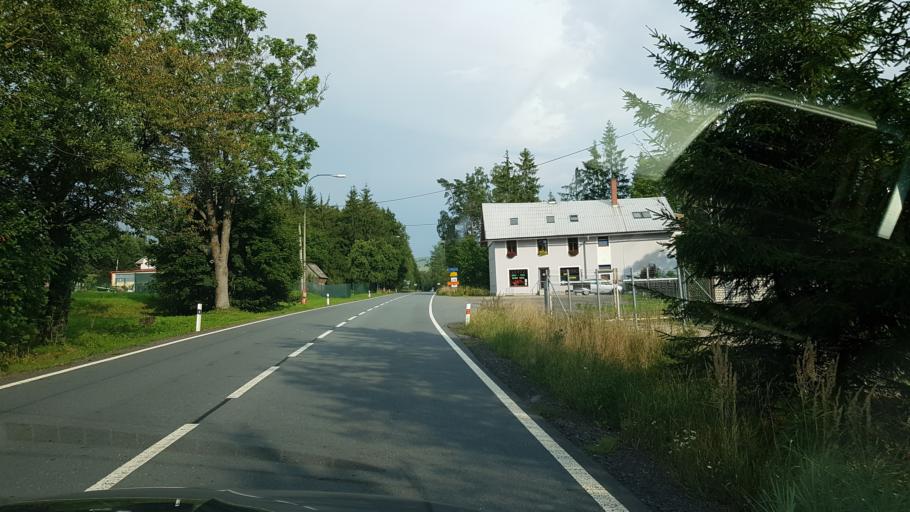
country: CZ
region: Pardubicky
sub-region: Okres Usti nad Orlici
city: Kraliky
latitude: 50.0886
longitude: 16.7229
